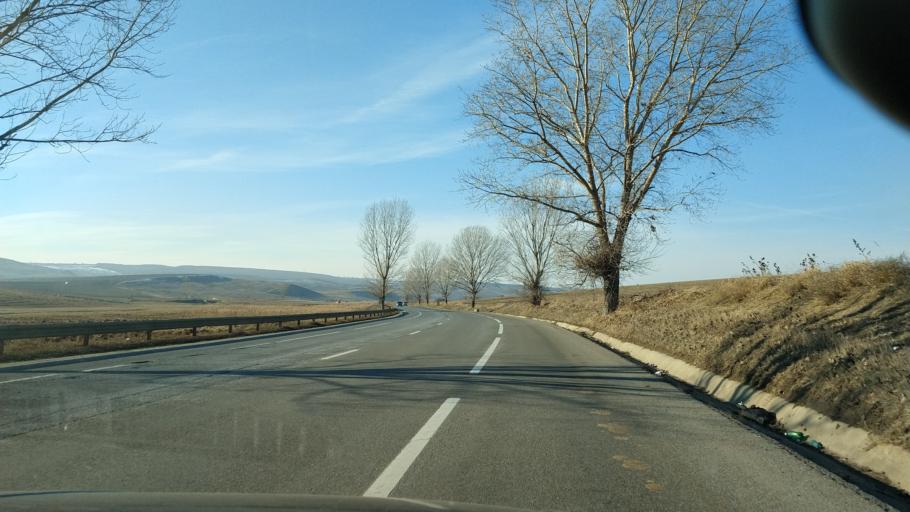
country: RO
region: Iasi
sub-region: Comuna Targu Frumos
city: Targu Frumos
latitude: 47.1980
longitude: 26.9822
